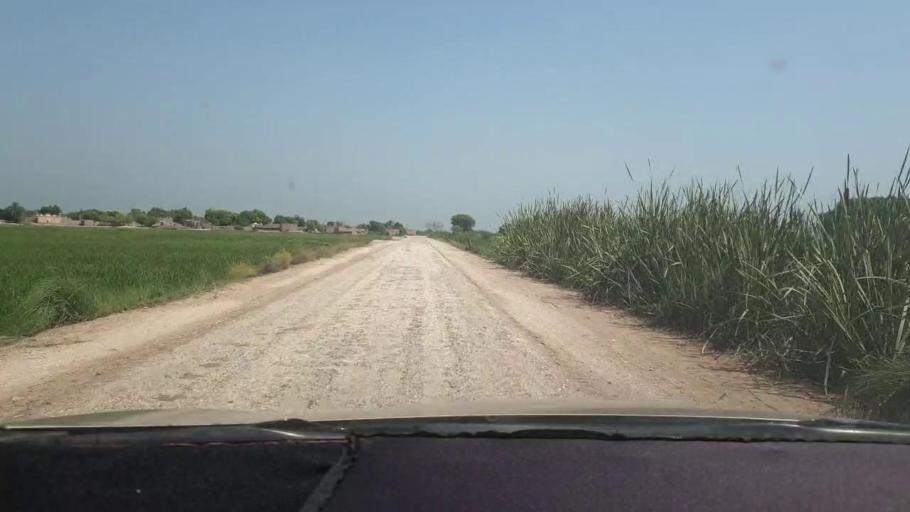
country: PK
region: Sindh
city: Miro Khan
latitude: 27.6858
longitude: 68.0908
